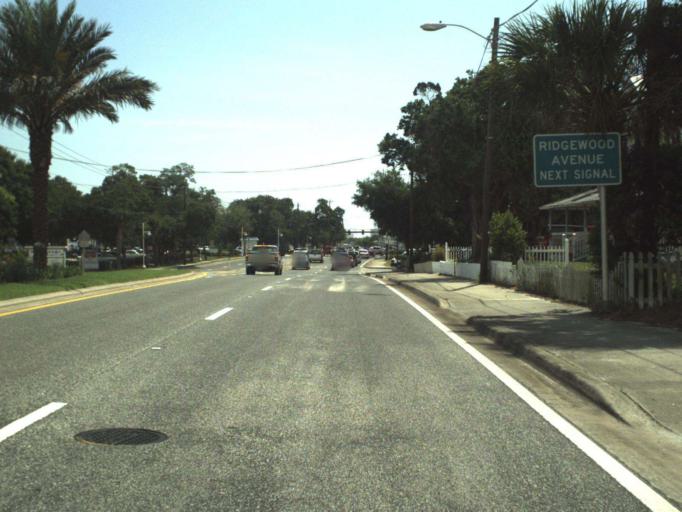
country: US
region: Florida
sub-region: Volusia County
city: Port Orange
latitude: 29.1429
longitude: -80.9905
